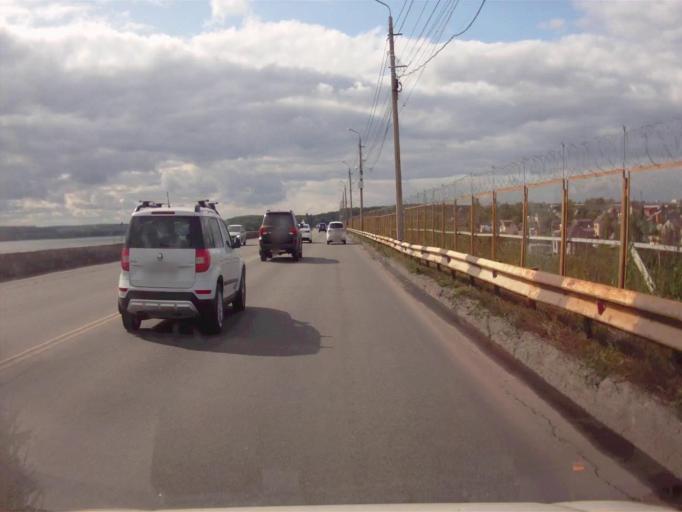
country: RU
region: Chelyabinsk
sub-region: Gorod Chelyabinsk
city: Chelyabinsk
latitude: 55.1461
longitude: 61.3144
